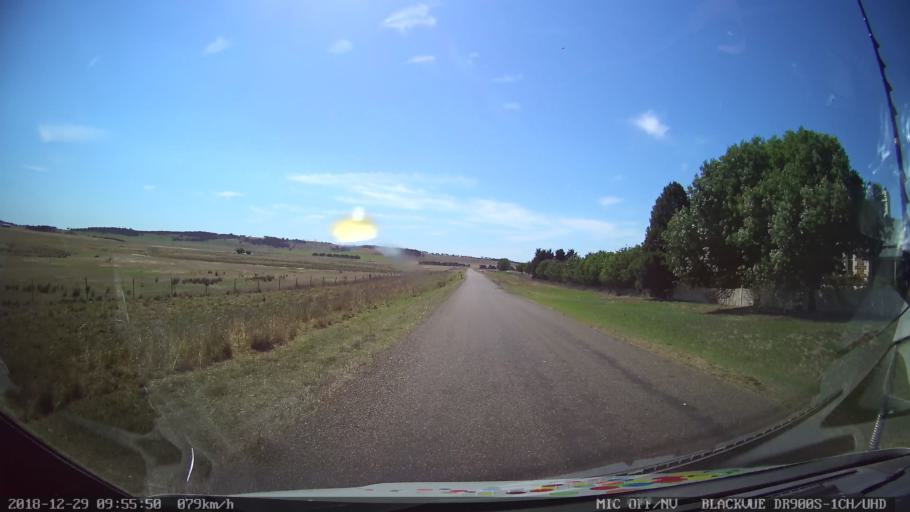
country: AU
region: New South Wales
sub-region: Goulburn Mulwaree
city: Goulburn
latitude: -34.7737
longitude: 149.4724
